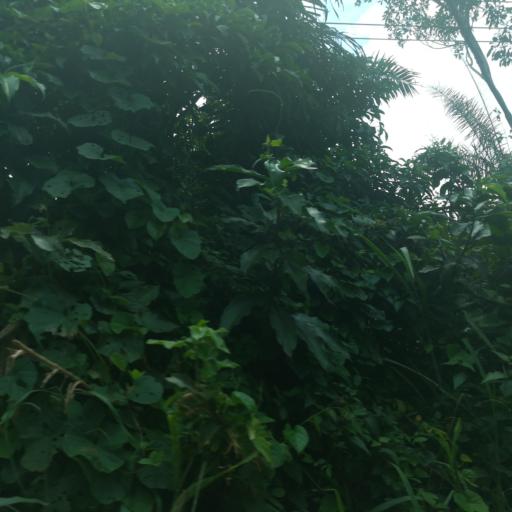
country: NG
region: Lagos
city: Ejirin
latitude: 6.6305
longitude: 3.7080
